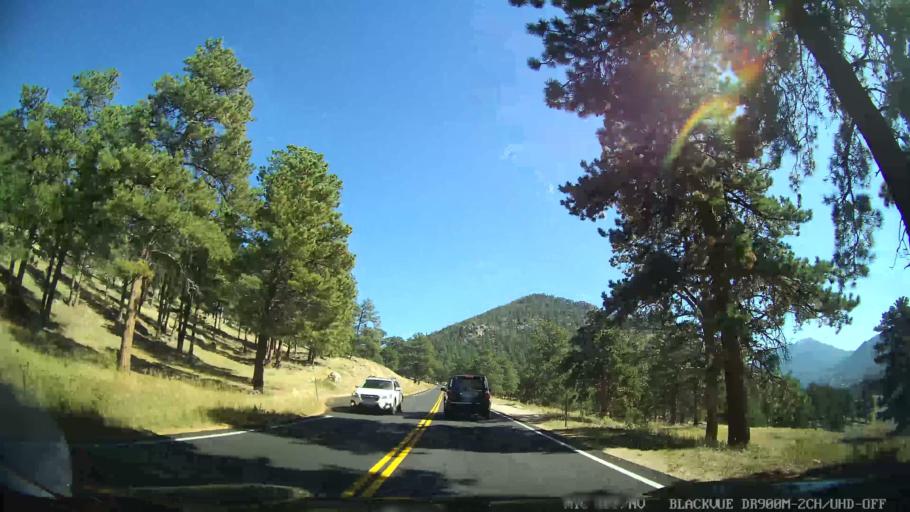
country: US
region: Colorado
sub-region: Larimer County
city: Estes Park
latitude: 40.3602
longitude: -105.5867
